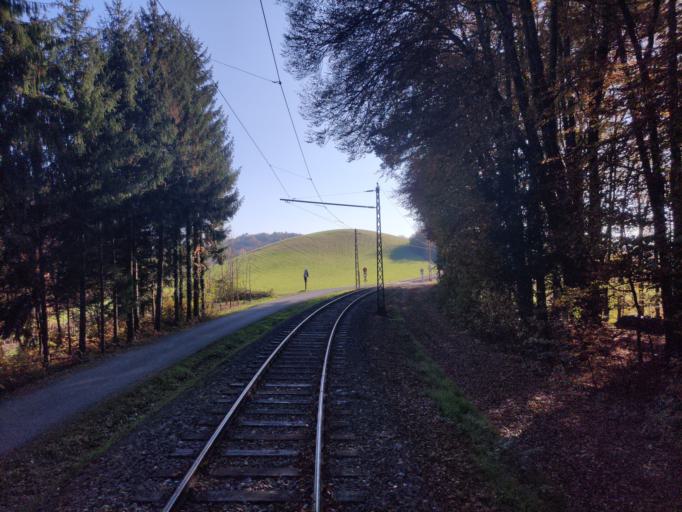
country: AT
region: Styria
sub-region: Politischer Bezirk Suedoststeiermark
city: Maierdorf
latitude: 46.8998
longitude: 15.8330
